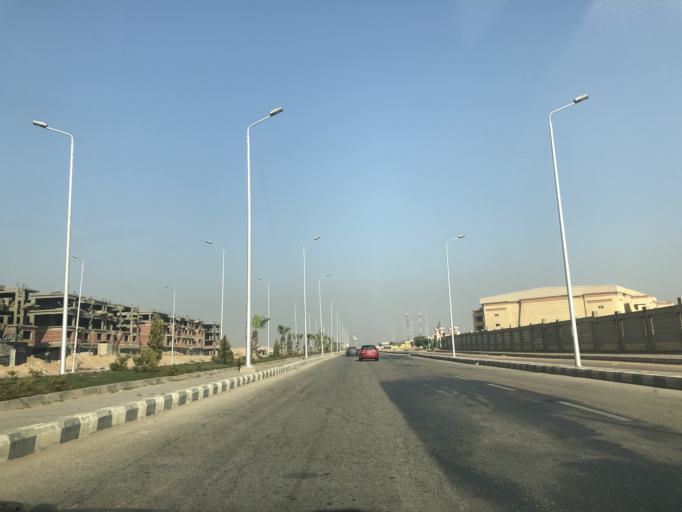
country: EG
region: Al Jizah
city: Madinat Sittah Uktubar
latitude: 29.9512
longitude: 31.0719
